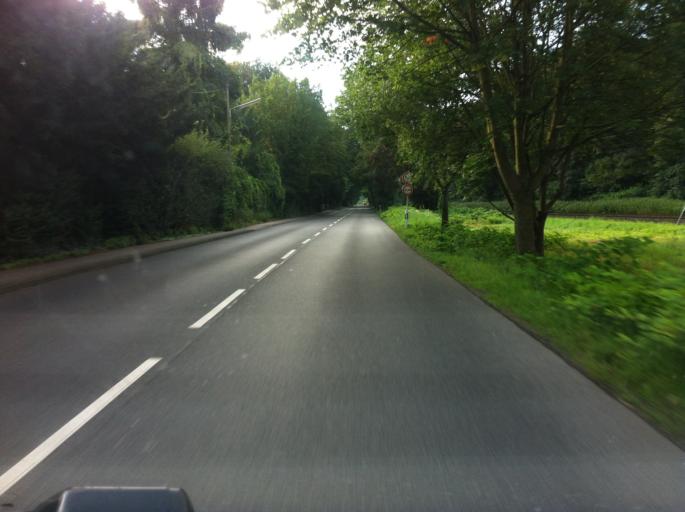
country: DE
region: North Rhine-Westphalia
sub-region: Regierungsbezirk Koln
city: Mengenich
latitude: 50.9749
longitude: 6.8608
